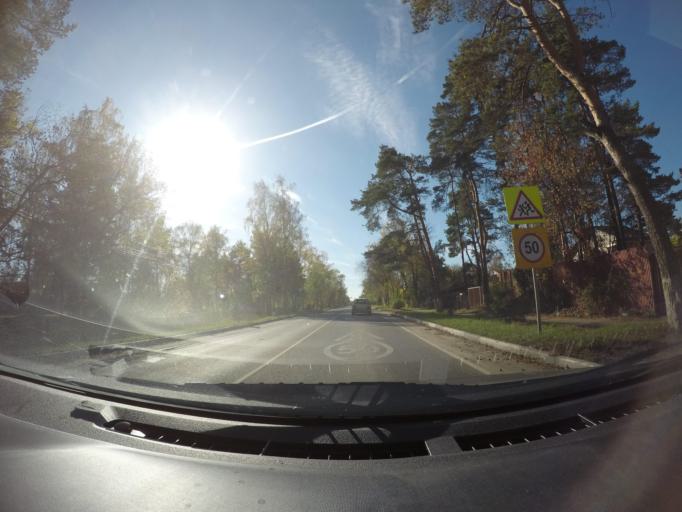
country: RU
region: Moskovskaya
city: Rodniki
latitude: 55.6551
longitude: 38.0585
